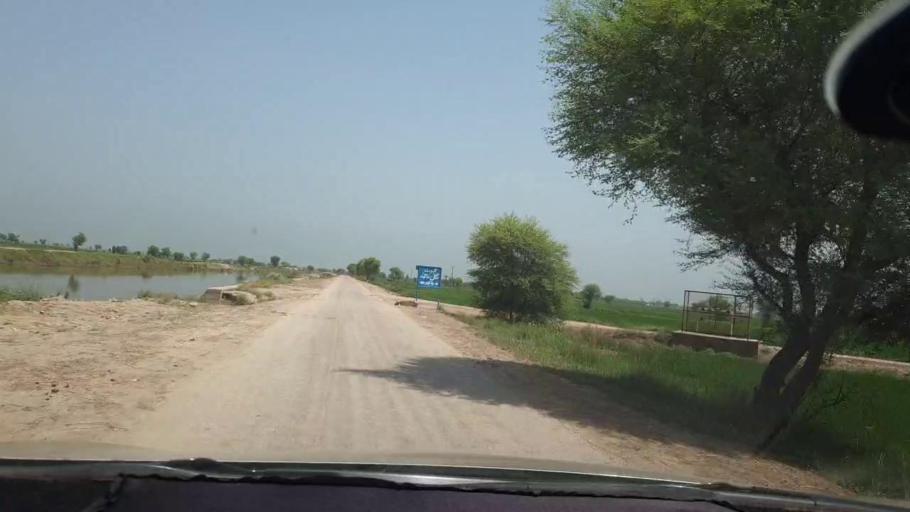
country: PK
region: Sindh
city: Kambar
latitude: 27.6865
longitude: 67.9364
